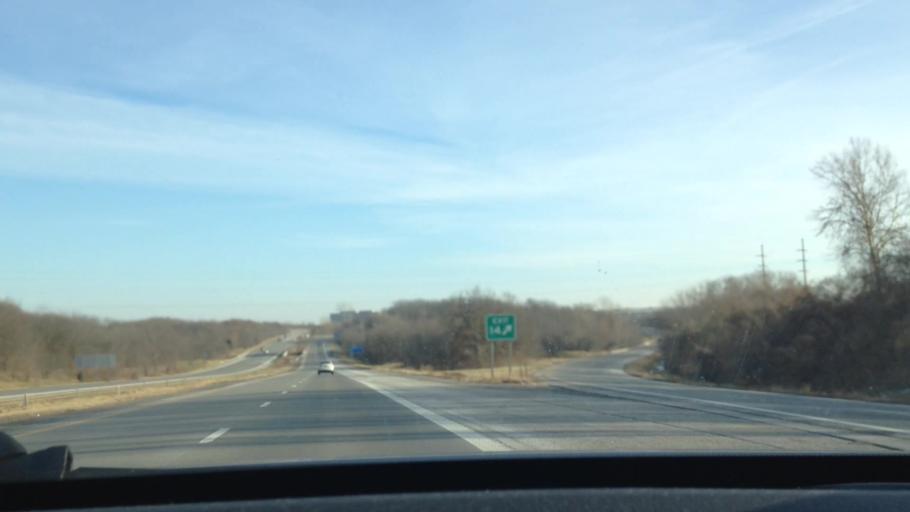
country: US
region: Missouri
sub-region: Platte County
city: Weatherby Lake
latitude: 39.3246
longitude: -94.7037
